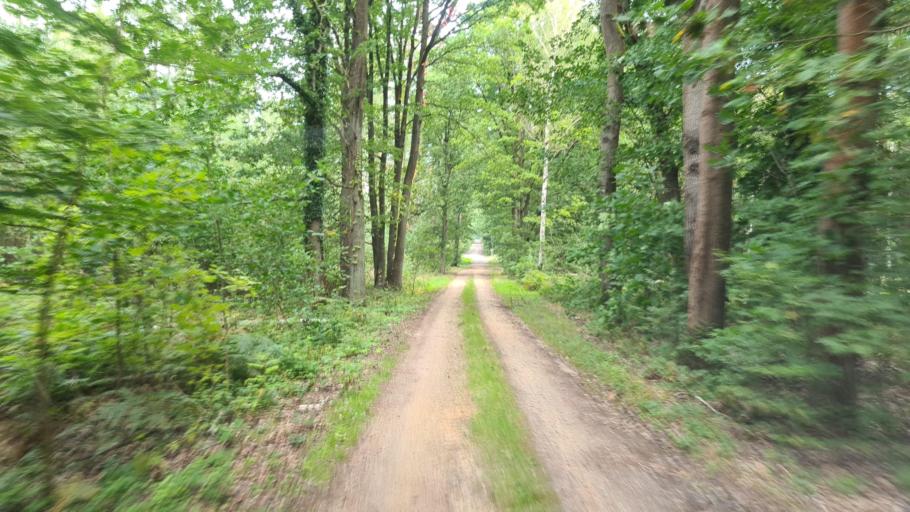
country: DE
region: Brandenburg
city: Hohenbucko
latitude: 51.7952
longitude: 13.5323
